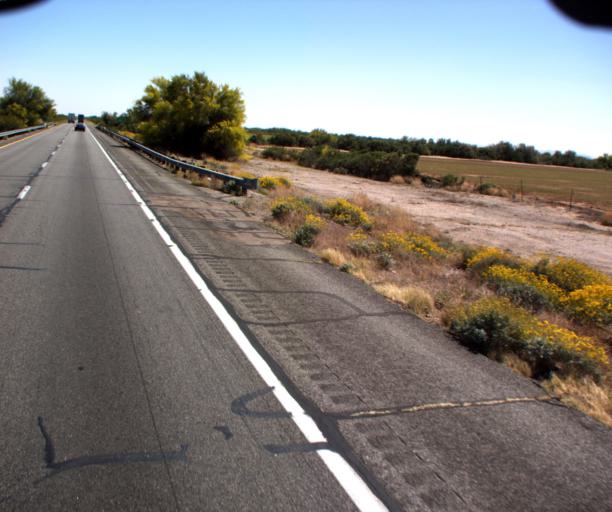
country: US
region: Arizona
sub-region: Maricopa County
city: Buckeye
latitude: 33.4887
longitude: -112.8987
